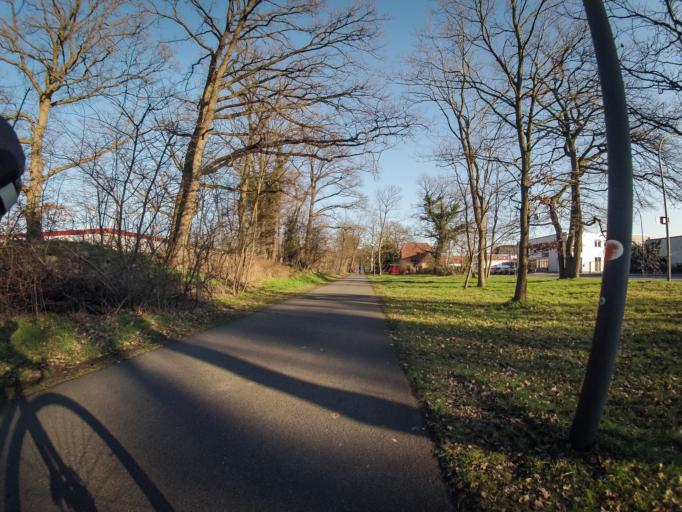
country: DE
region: Lower Saxony
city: Wallenhorst
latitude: 52.3046
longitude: 8.0050
